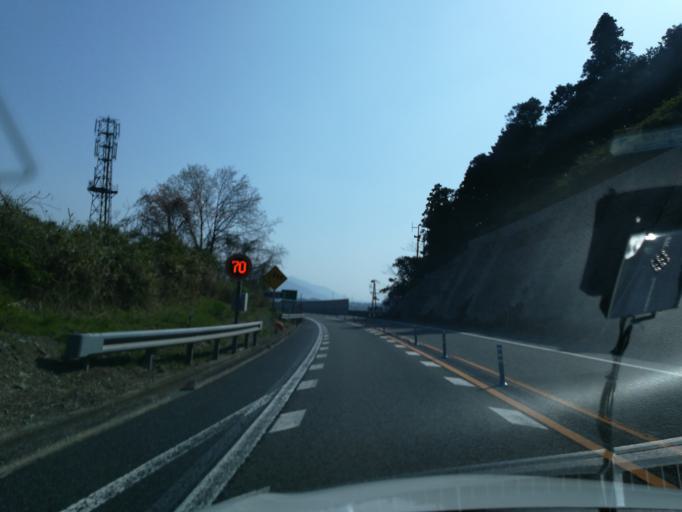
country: JP
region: Tokushima
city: Ikedacho
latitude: 34.0317
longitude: 133.8596
